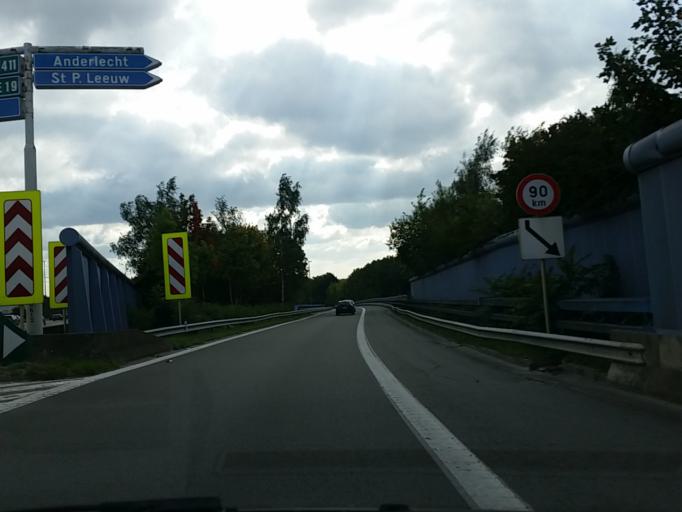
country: BE
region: Flanders
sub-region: Provincie Vlaams-Brabant
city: Dilbeek
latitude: 50.8169
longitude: 4.2861
